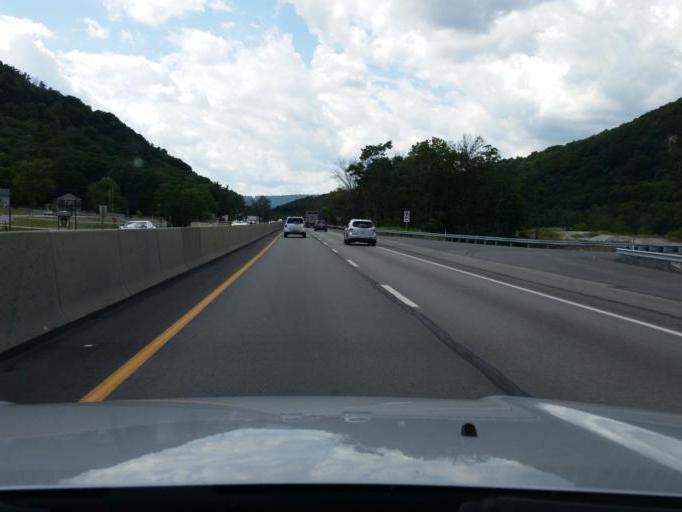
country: US
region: Pennsylvania
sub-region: Bedford County
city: Everett
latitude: 40.0062
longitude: -78.3843
